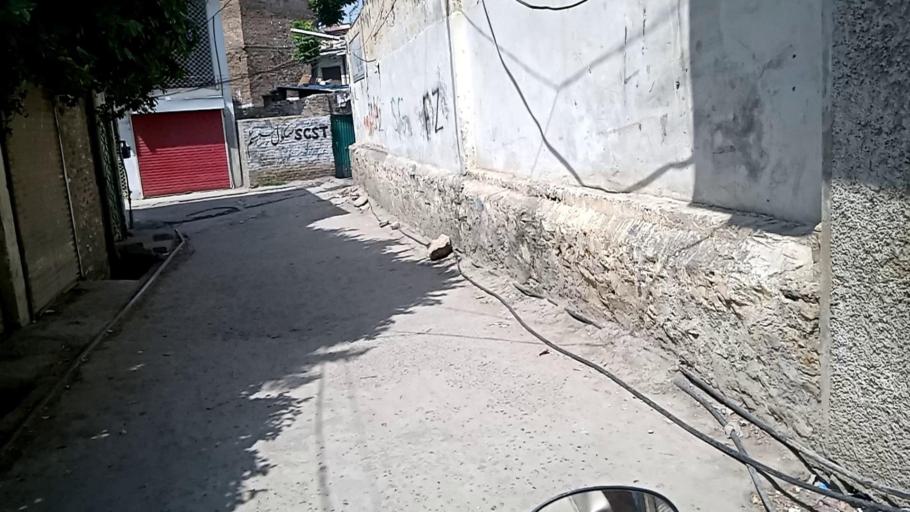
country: PK
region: Khyber Pakhtunkhwa
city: Mingora
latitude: 34.7759
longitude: 72.3567
